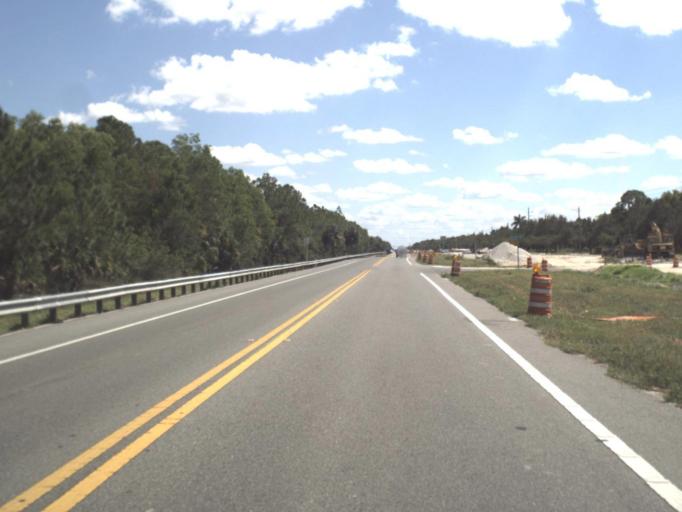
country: US
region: Florida
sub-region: Collier County
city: Lely Resort
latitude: 26.0565
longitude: -81.6884
